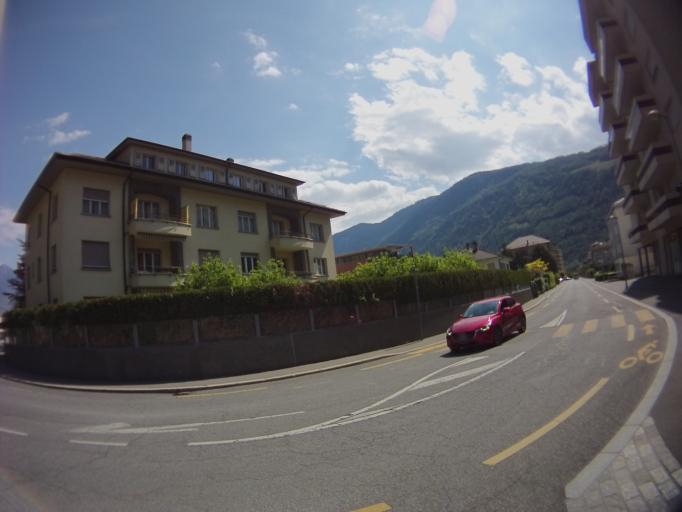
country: CH
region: Valais
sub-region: Martigny District
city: Martigny-Ville
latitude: 46.1008
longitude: 7.0685
